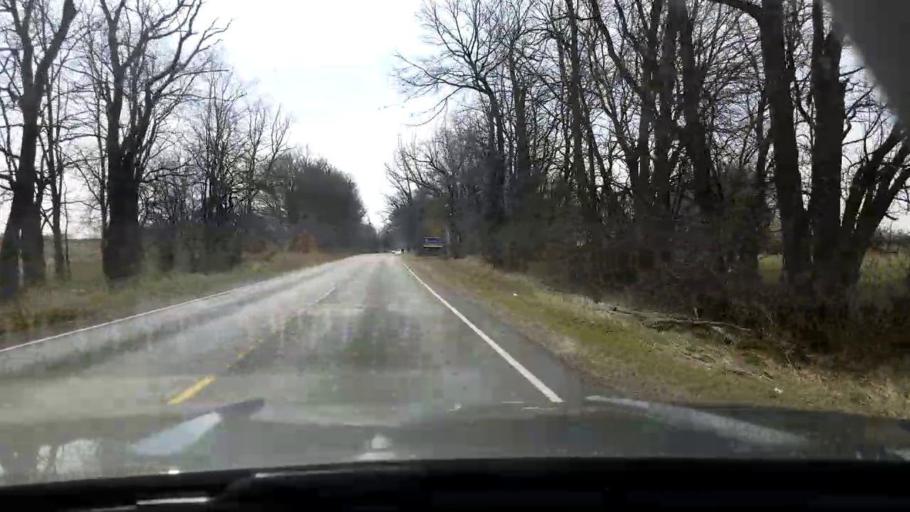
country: US
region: Michigan
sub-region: Jackson County
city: Spring Arbor
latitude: 42.1719
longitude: -84.5200
